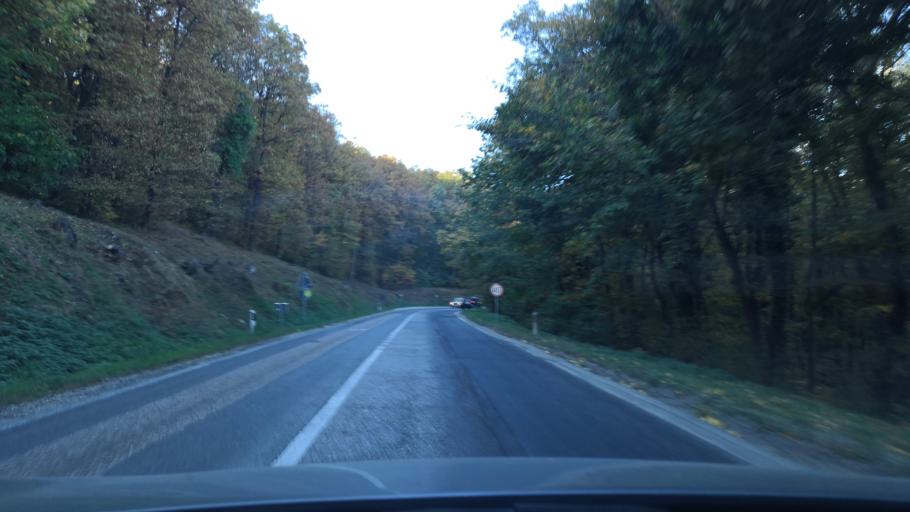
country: RS
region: Autonomna Pokrajina Vojvodina
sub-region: Sremski Okrug
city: Irig
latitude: 45.1405
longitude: 19.8370
